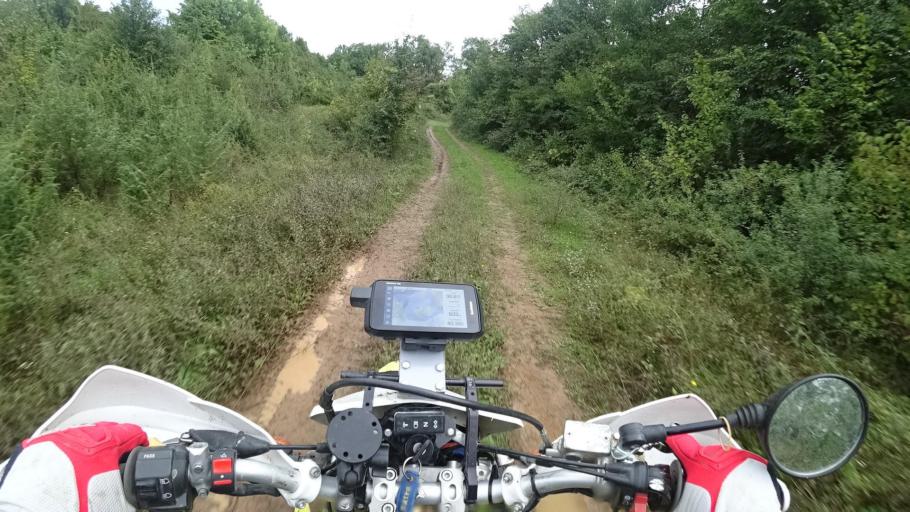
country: BA
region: Republika Srpska
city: Bronzani Majdan
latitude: 44.6466
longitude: 17.0202
